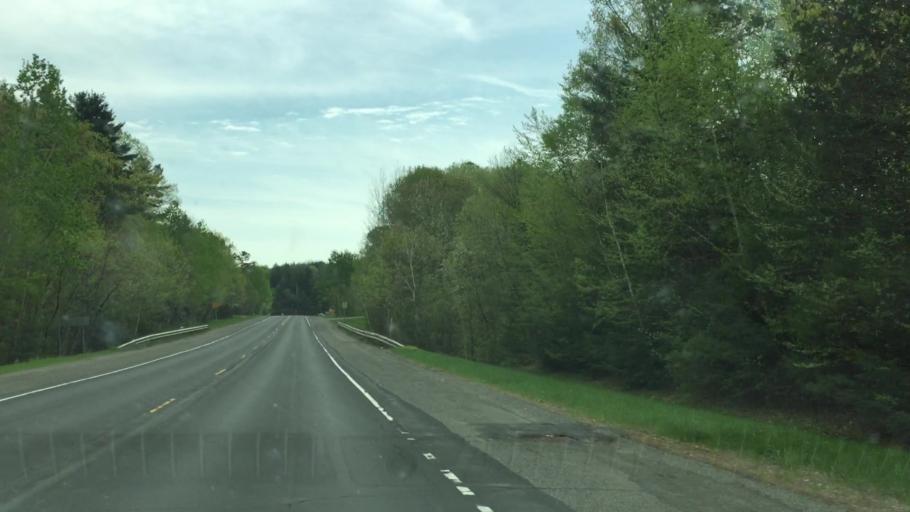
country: US
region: Massachusetts
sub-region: Berkshire County
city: Pittsfield
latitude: 42.4121
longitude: -73.2689
